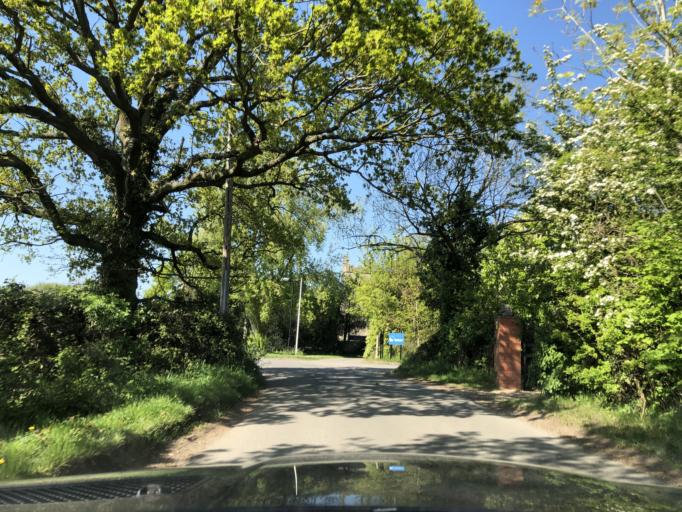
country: GB
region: England
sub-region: Warwickshire
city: Warwick
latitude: 52.2867
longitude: -1.6227
